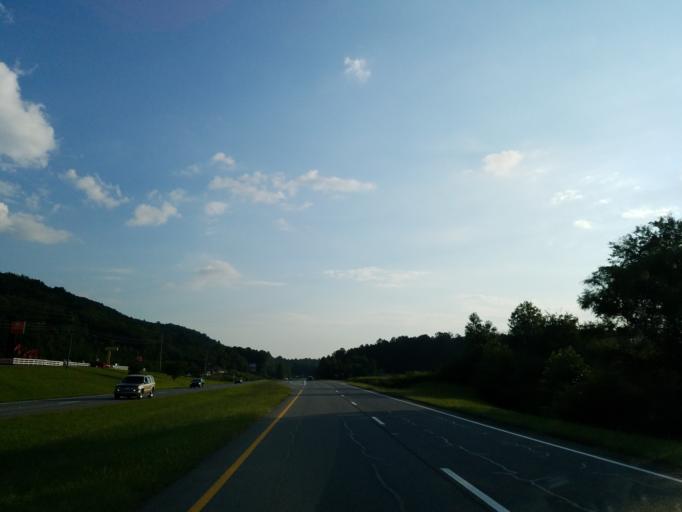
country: US
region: Georgia
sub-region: Fannin County
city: Blue Ridge
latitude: 34.8366
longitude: -84.3415
